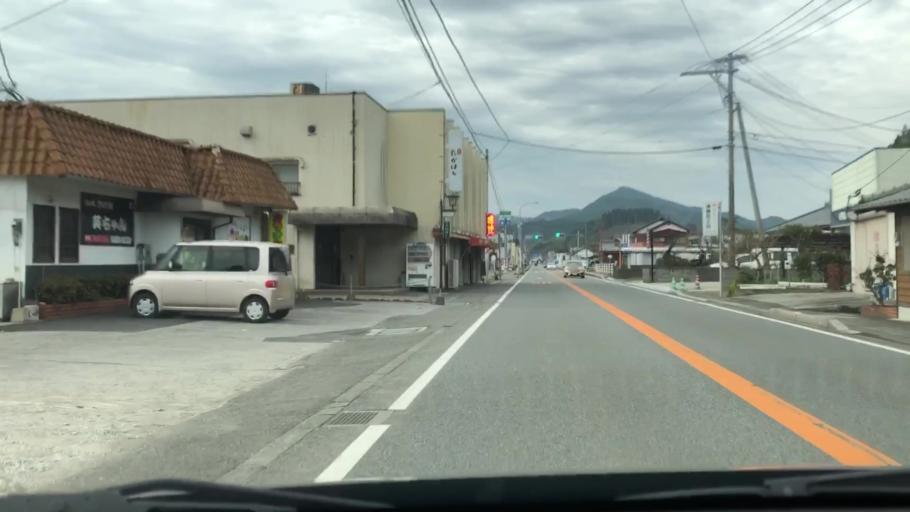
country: JP
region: Oita
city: Saiki
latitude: 32.9753
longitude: 131.8438
